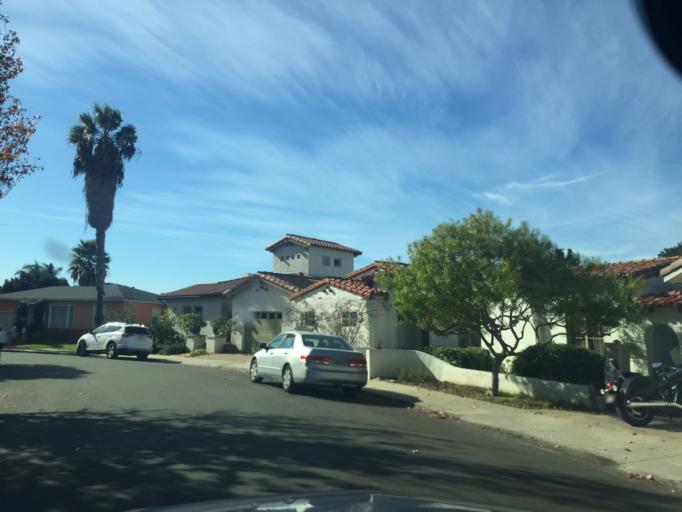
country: US
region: California
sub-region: San Diego County
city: Lemon Grove
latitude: 32.7675
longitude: -117.1013
